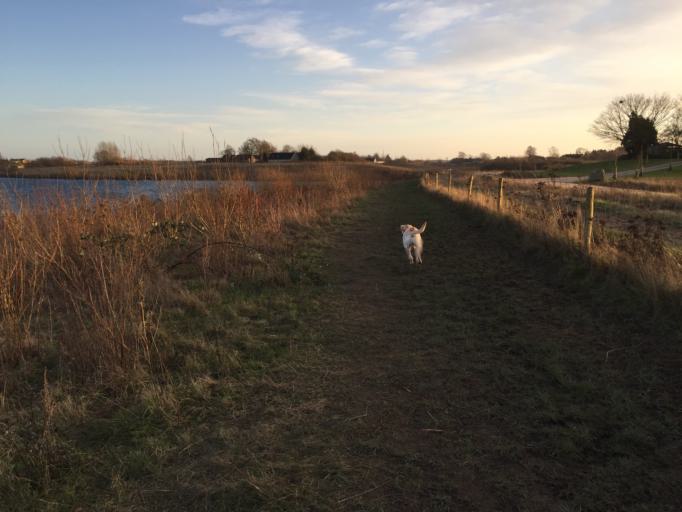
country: DK
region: South Denmark
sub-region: Kerteminde Kommune
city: Langeskov
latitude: 55.3300
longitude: 10.5263
